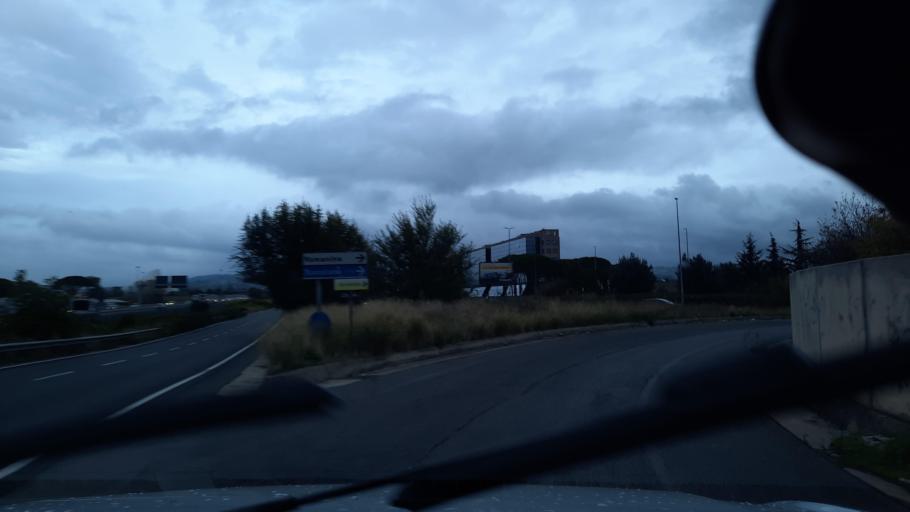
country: IT
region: Latium
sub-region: Citta metropolitana di Roma Capitale
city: Ciampino
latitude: 41.8473
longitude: 12.6126
